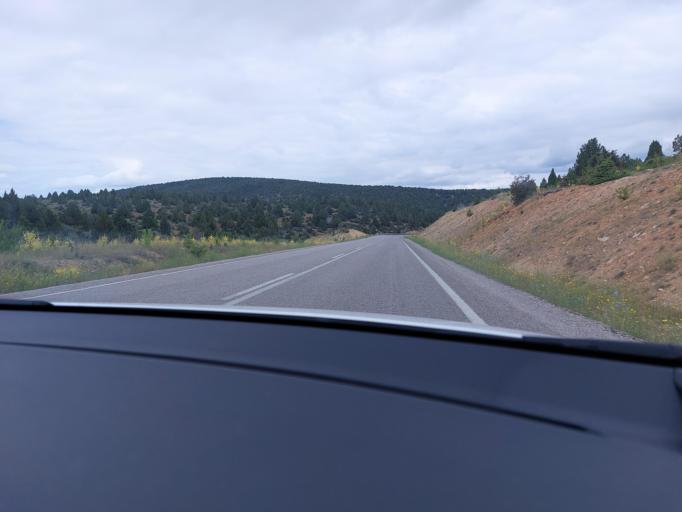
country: TR
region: Konya
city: Doganbey
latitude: 37.8853
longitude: 31.8273
